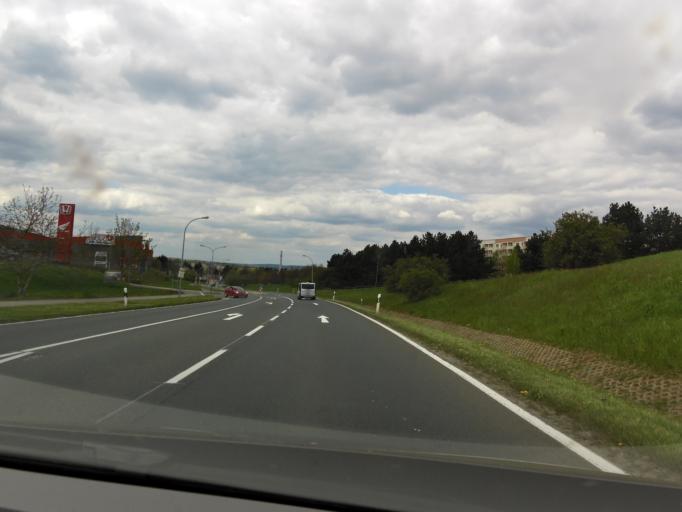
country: DE
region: Saxony-Anhalt
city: Weissenfels
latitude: 51.1895
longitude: 11.9843
